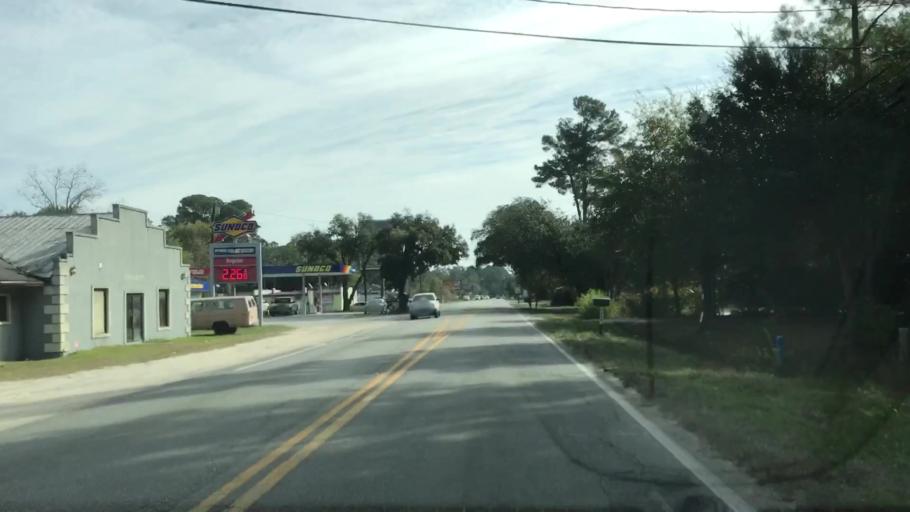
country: US
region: South Carolina
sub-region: Colleton County
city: Walterboro
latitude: 32.8965
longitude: -80.6433
